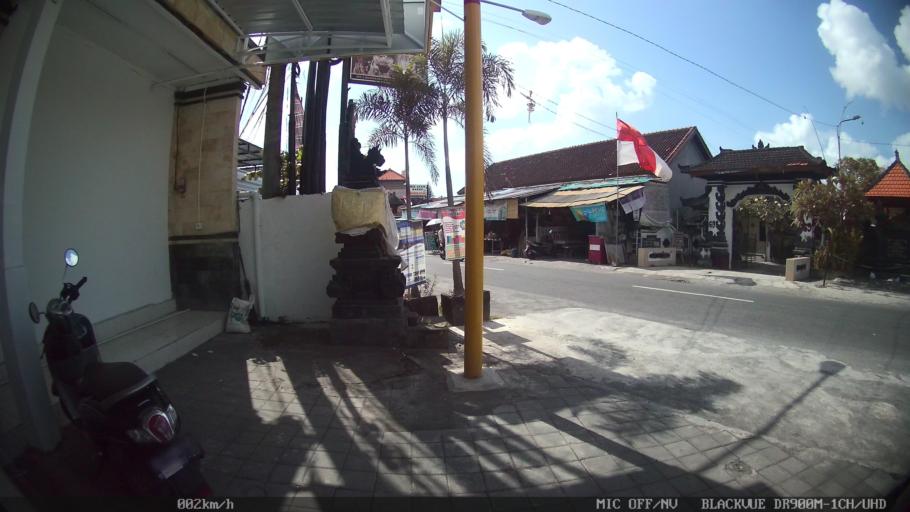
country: ID
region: Bali
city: Jabajero
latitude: -8.7192
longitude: 115.1924
